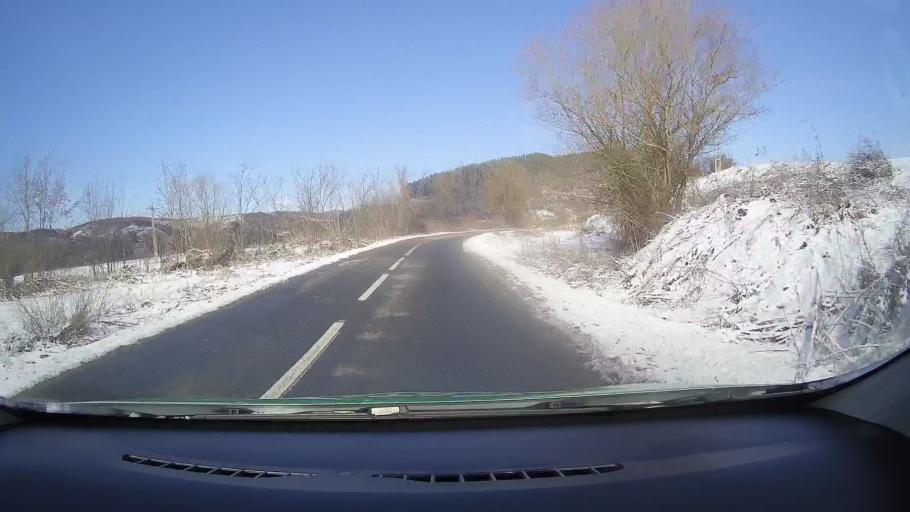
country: RO
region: Sibiu
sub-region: Comuna Mihaileni
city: Mihaileni
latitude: 46.0044
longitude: 24.3621
